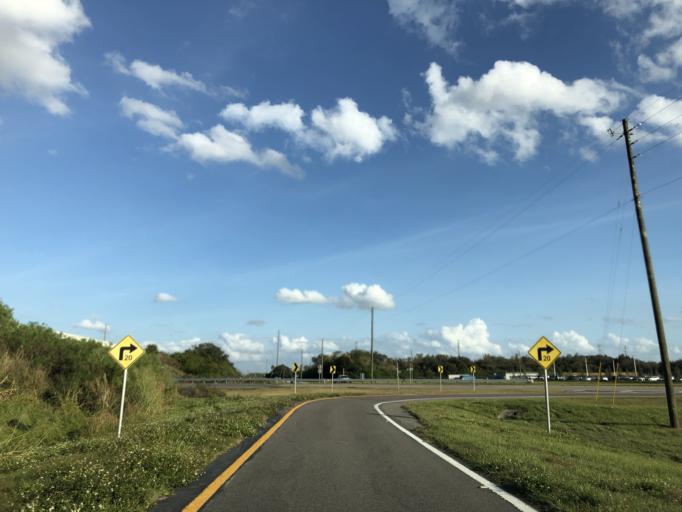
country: US
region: Florida
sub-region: Orange County
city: Tangelo Park
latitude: 28.4497
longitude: -81.4603
